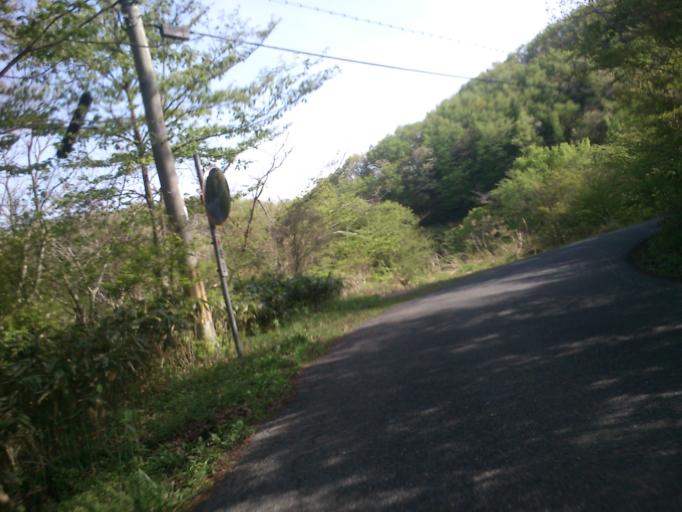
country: JP
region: Kyoto
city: Miyazu
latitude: 35.6480
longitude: 135.1801
